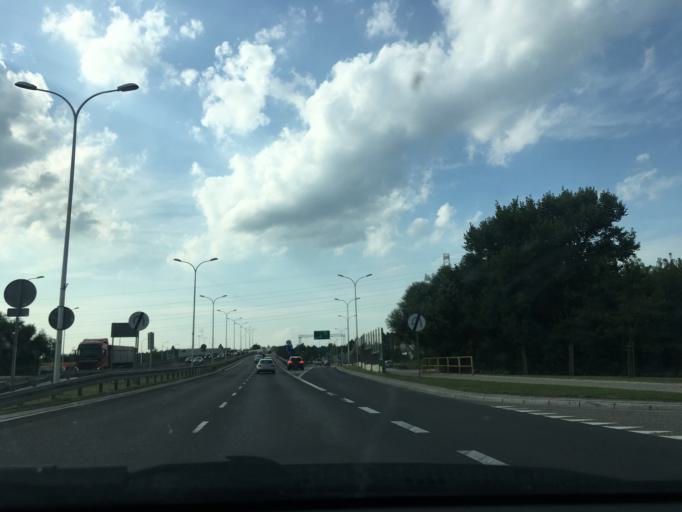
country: PL
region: Podlasie
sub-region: Bialystok
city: Bialystok
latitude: 53.1569
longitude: 23.1557
